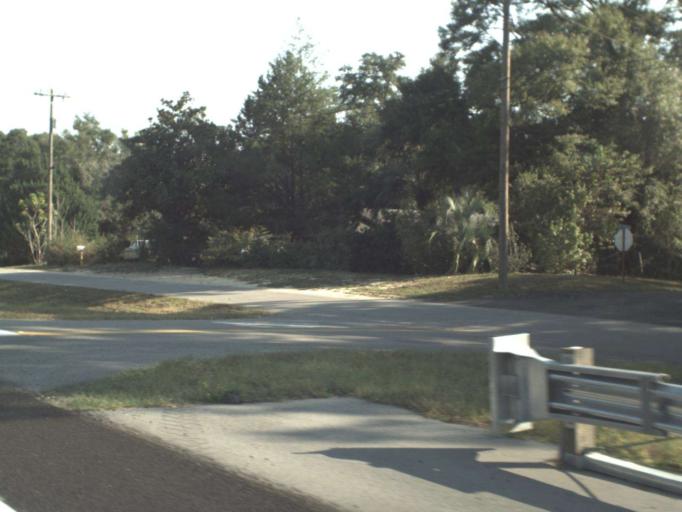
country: US
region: Florida
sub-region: Bay County
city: Laguna Beach
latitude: 30.5019
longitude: -85.8411
